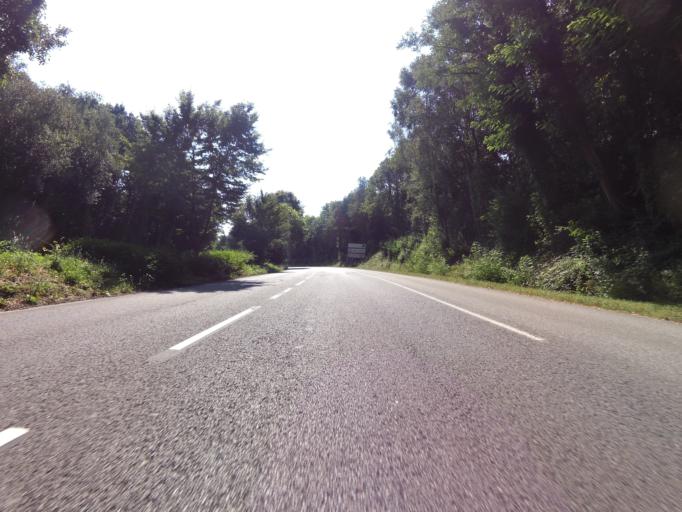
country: FR
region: Brittany
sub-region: Departement du Finistere
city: Quimper
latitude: 47.9811
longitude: -4.1093
